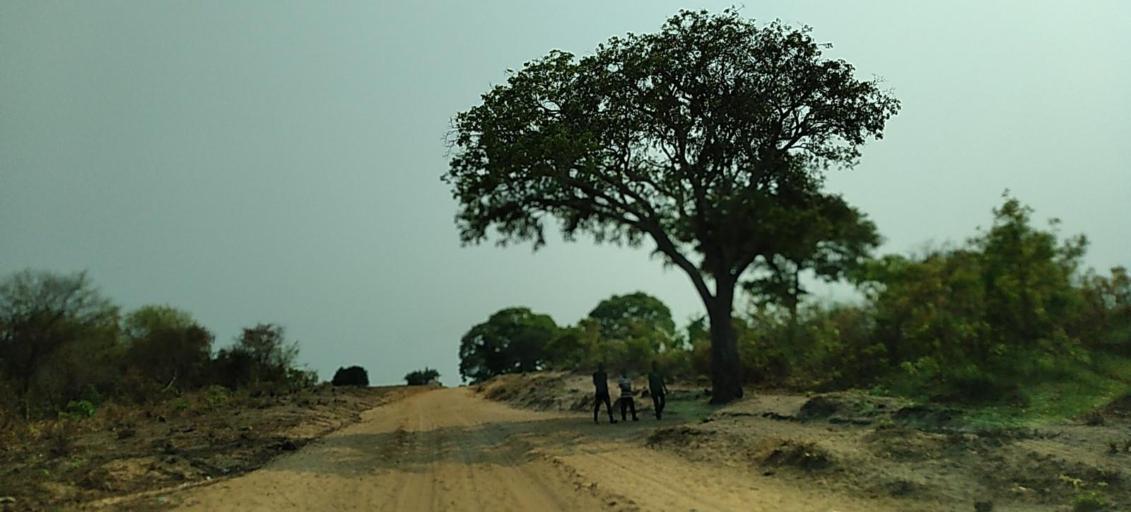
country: ZM
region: North-Western
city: Zambezi
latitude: -13.1772
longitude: 23.4017
